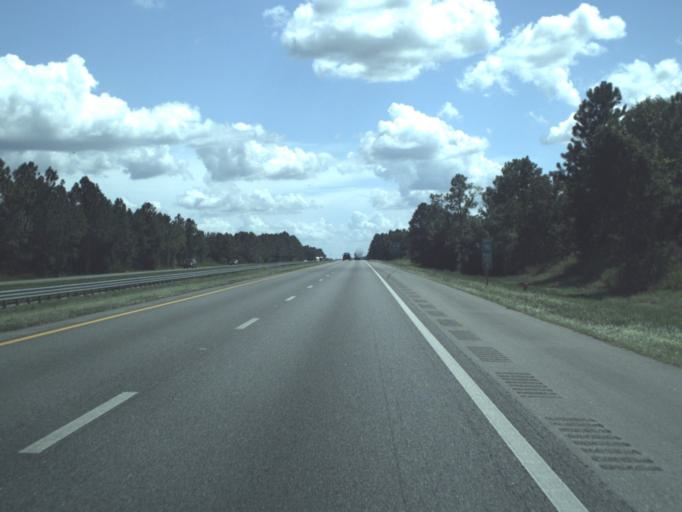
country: US
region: Florida
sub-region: Hernando County
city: Hill 'n Dale
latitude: 28.5451
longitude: -82.2372
